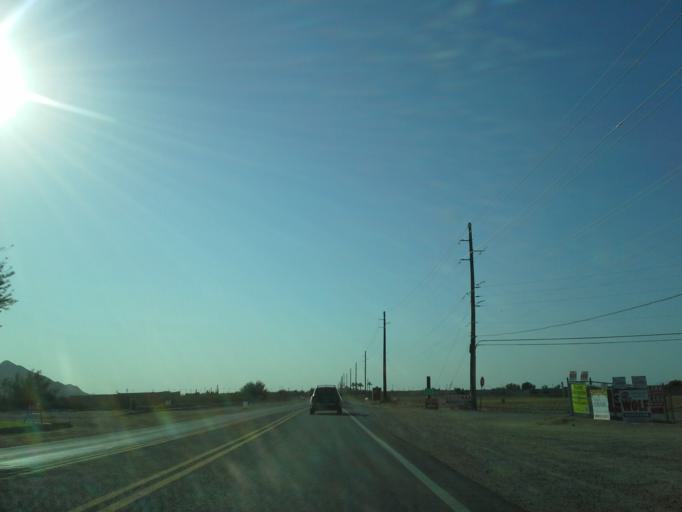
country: US
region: Arizona
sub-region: Pinal County
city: San Tan Valley
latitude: 33.1725
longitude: -111.5749
